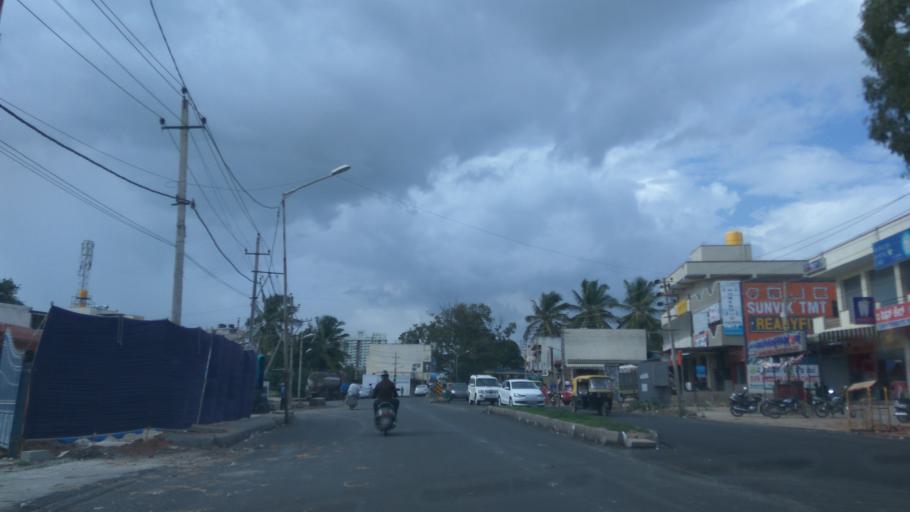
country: IN
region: Karnataka
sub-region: Bangalore Urban
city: Yelahanka
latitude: 13.0545
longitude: 77.6319
